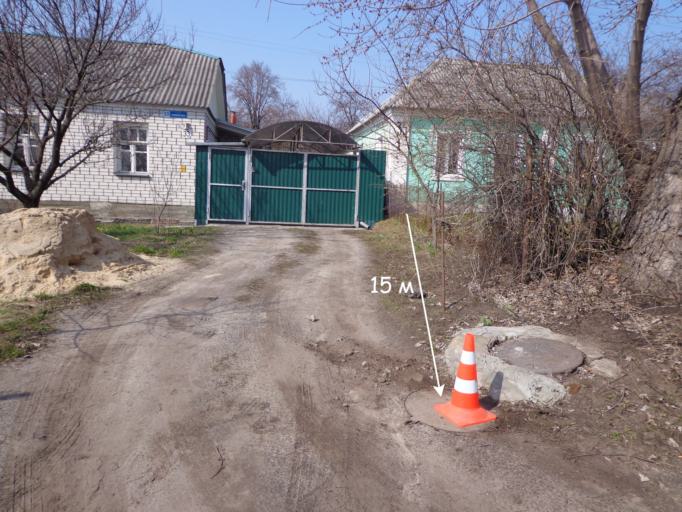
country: RU
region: Voronezj
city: Voronezh
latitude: 51.7028
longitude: 39.2333
